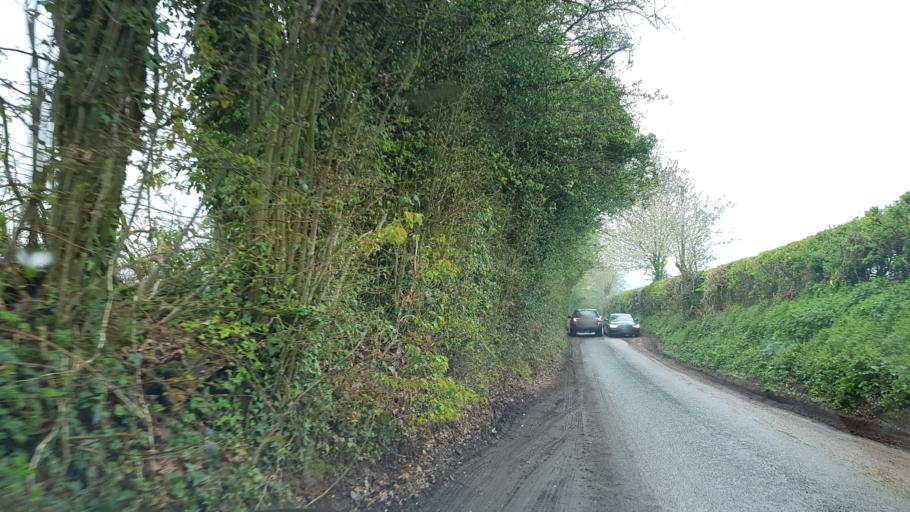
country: GB
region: England
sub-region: Herefordshire
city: Ledbury
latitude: 52.0679
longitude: -2.4288
